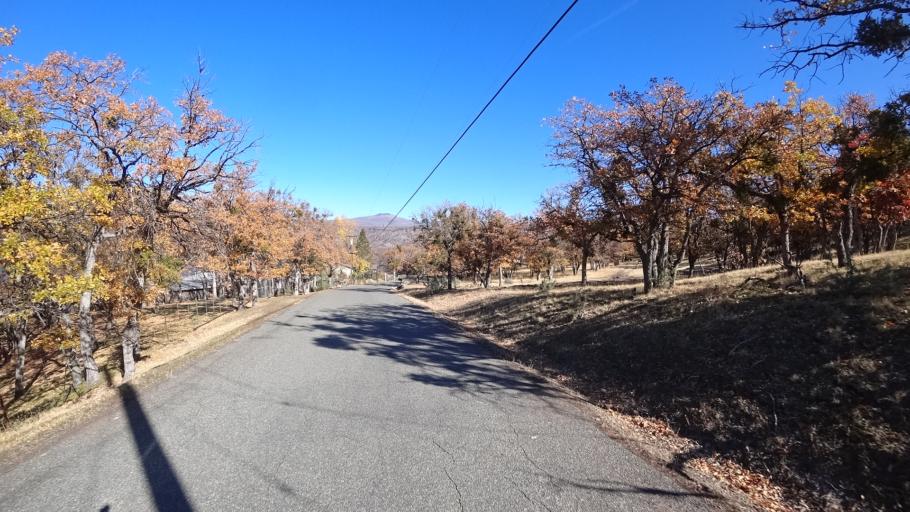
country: US
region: California
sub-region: Siskiyou County
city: Montague
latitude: 41.9785
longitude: -122.3167
